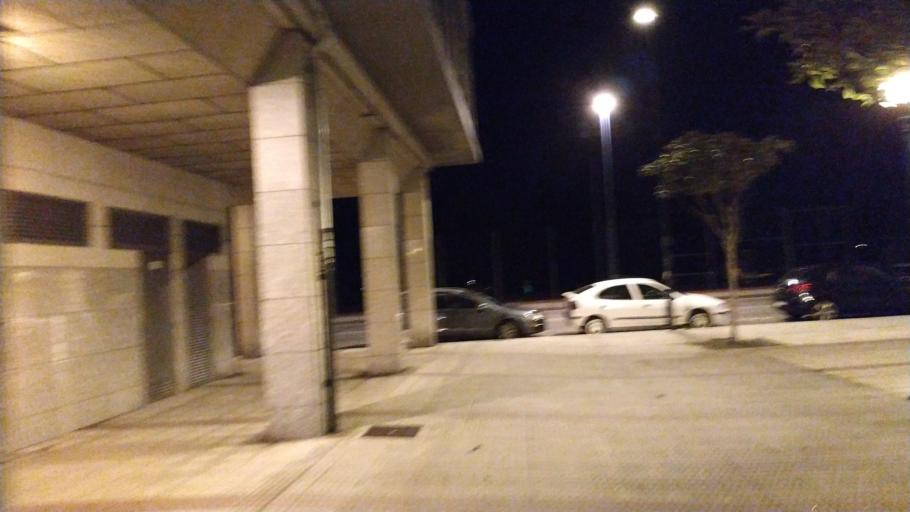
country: ES
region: Galicia
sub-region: Provincia da Coruna
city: Cambre
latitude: 43.3184
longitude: -8.3674
